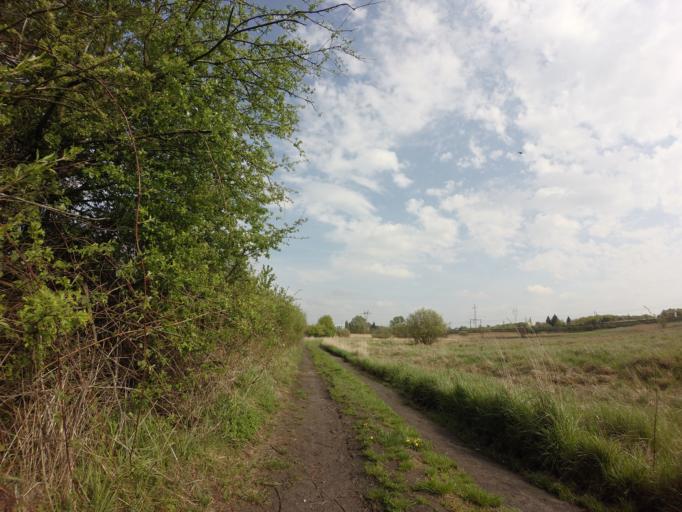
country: PL
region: West Pomeranian Voivodeship
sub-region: Powiat choszczenski
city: Choszczno
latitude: 53.1702
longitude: 15.3916
